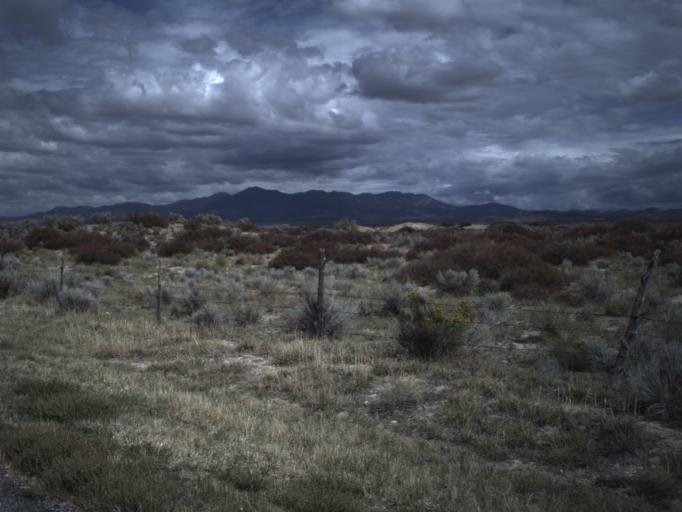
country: US
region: Utah
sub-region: Millard County
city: Fillmore
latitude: 39.1165
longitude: -112.4094
